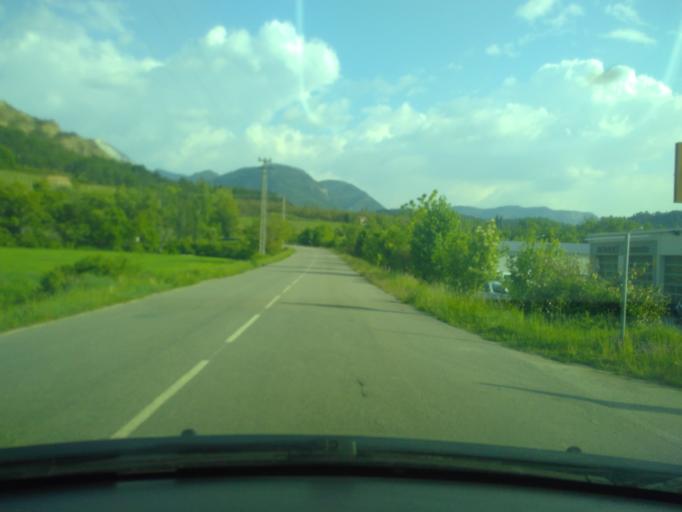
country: FR
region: Rhone-Alpes
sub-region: Departement de la Drome
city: Die
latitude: 44.6871
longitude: 5.4698
